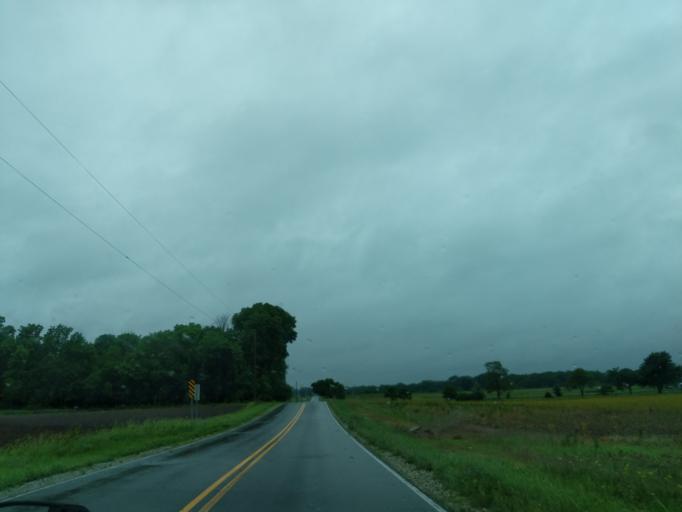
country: US
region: Indiana
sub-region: Madison County
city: Lapel
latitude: 40.0665
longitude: -85.9176
